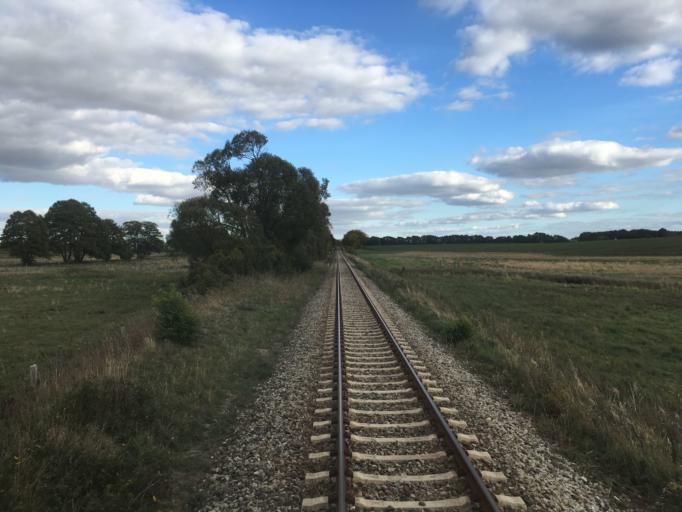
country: DE
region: Mecklenburg-Vorpommern
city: Grabowhofe
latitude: 53.5412
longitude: 12.5918
